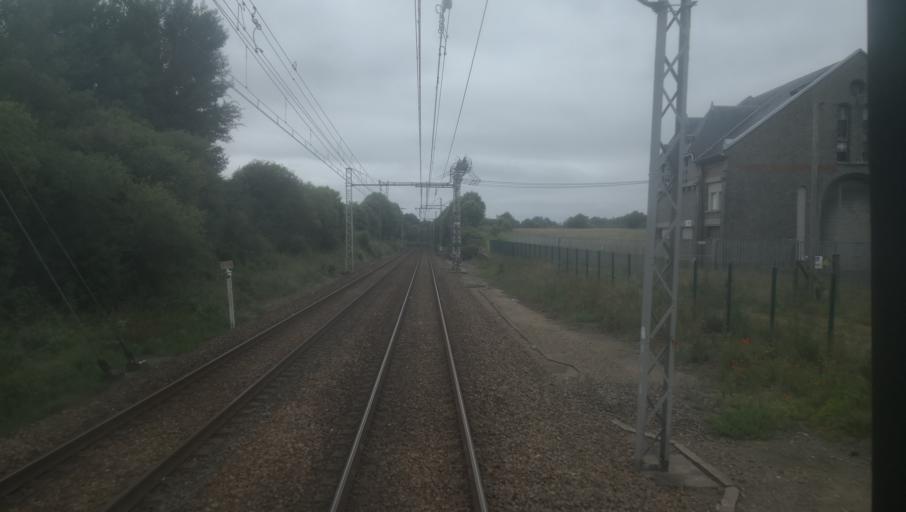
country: FR
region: Centre
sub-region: Departement de l'Indre
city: Chantome
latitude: 46.4440
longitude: 1.5523
